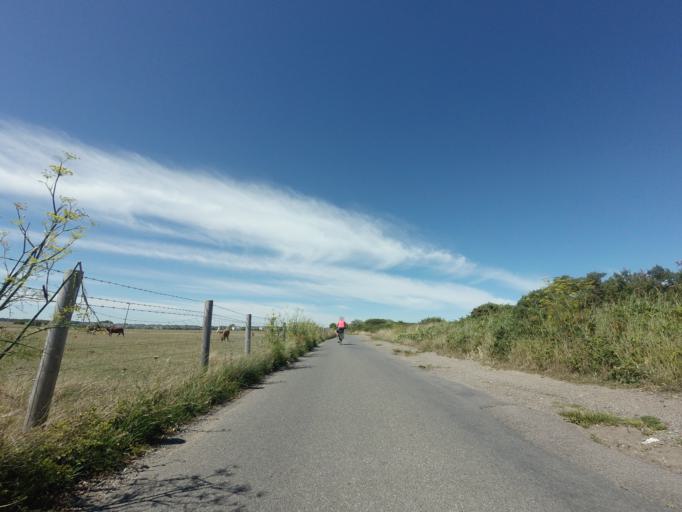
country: GB
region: England
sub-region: Kent
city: Deal
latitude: 51.2487
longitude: 1.3940
